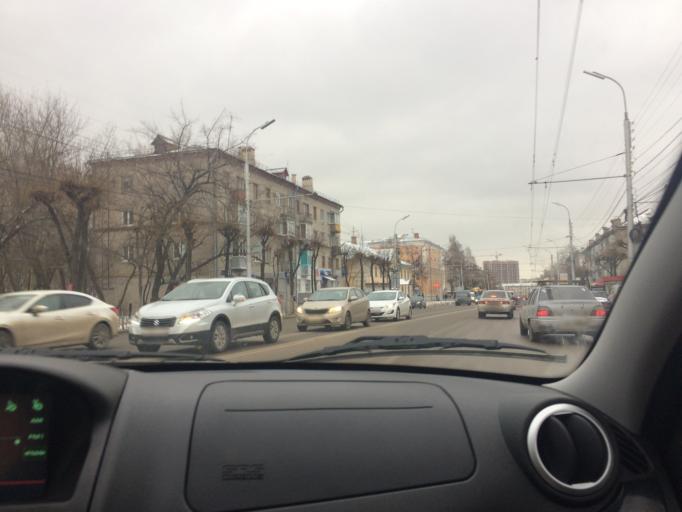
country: RU
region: Rjazan
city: Ryazan'
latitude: 54.6201
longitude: 39.7247
